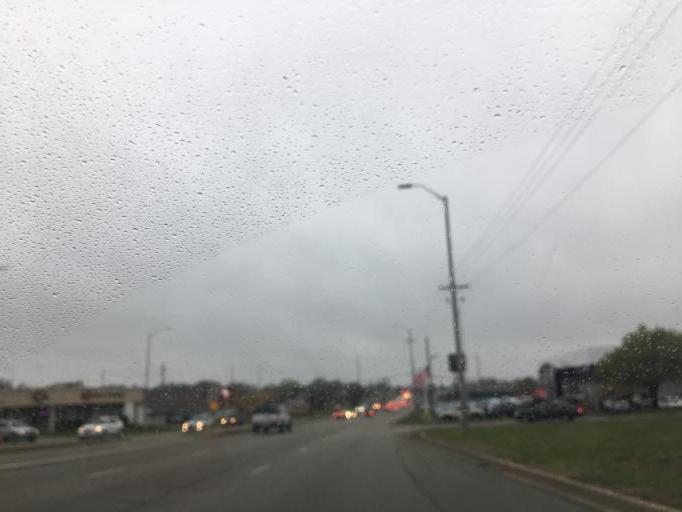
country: US
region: Kansas
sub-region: Johnson County
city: Olathe
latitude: 38.8839
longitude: -94.7935
